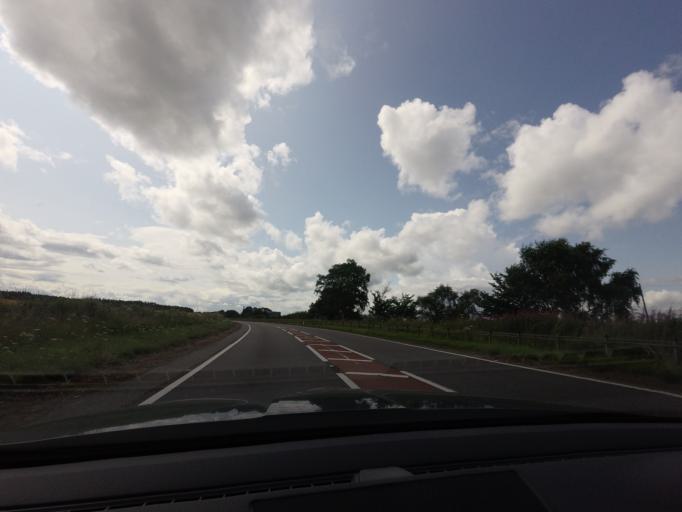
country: GB
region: Scotland
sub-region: Moray
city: Forres
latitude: 57.6023
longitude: -3.6598
